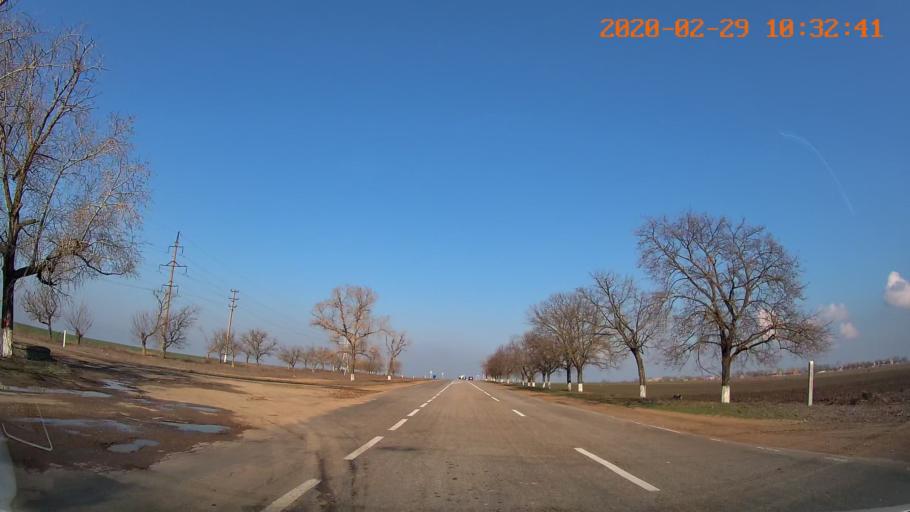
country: UA
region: Odessa
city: Velykoploske
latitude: 46.9638
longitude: 29.5520
